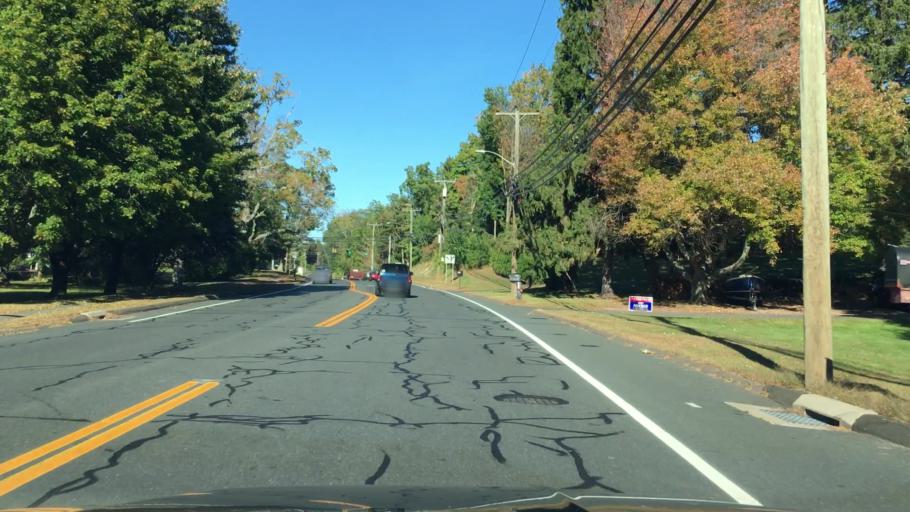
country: US
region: Connecticut
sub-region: Tolland County
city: Rockville
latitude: 41.8444
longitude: -72.4558
